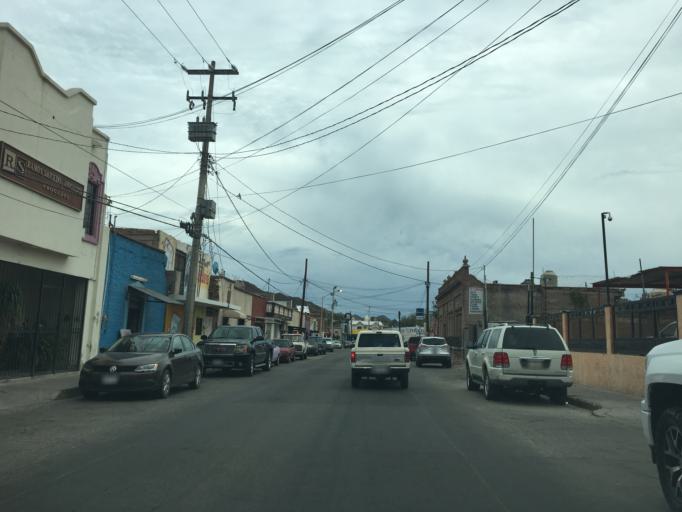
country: MX
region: Sonora
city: Heroica Guaymas
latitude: 27.9220
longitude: -110.8990
